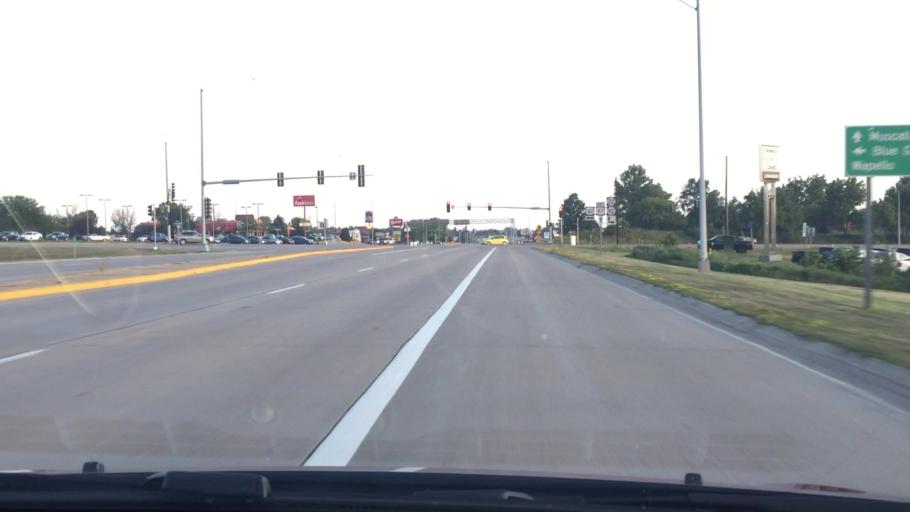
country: US
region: Iowa
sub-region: Muscatine County
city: Muscatine
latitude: 41.4548
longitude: -91.0303
